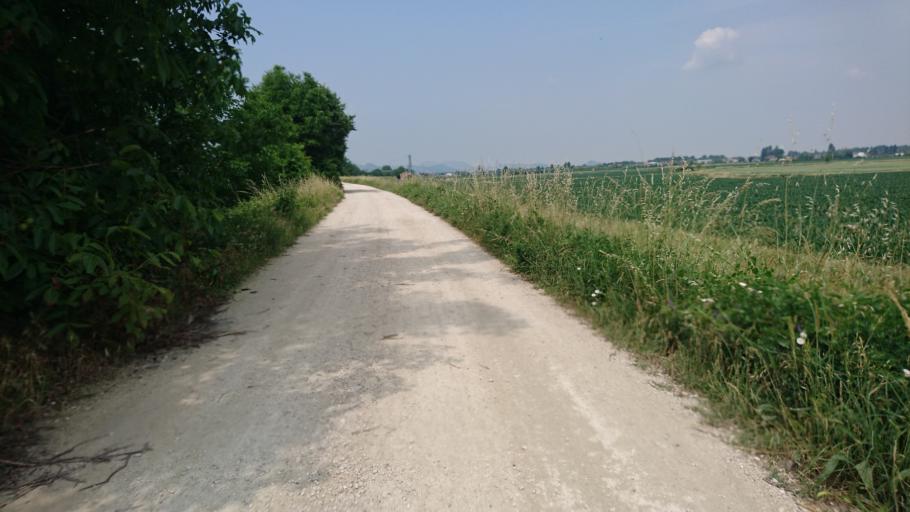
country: IT
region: Veneto
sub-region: Provincia di Padova
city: Terrassa Padovana
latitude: 45.2783
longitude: 11.9021
